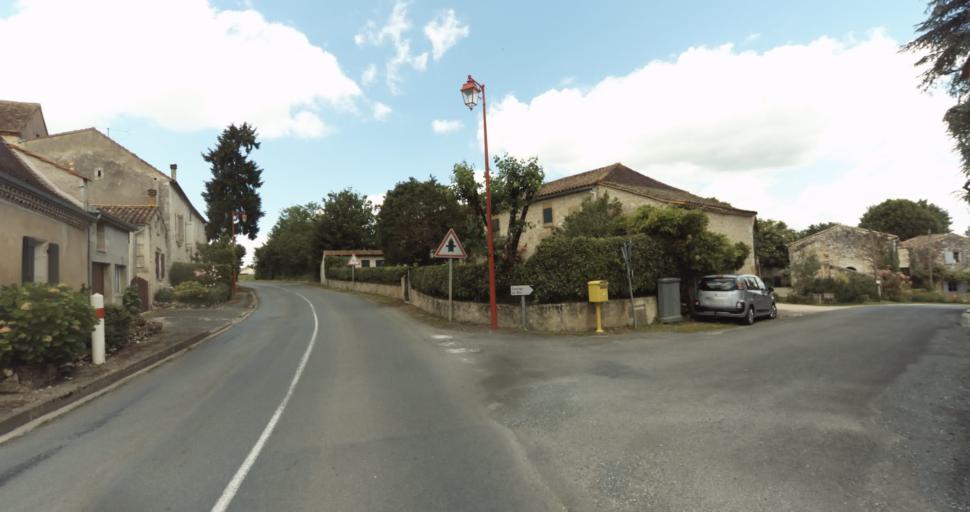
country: FR
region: Aquitaine
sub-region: Departement de la Dordogne
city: Beaumont-du-Perigord
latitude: 44.6957
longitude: 0.8638
